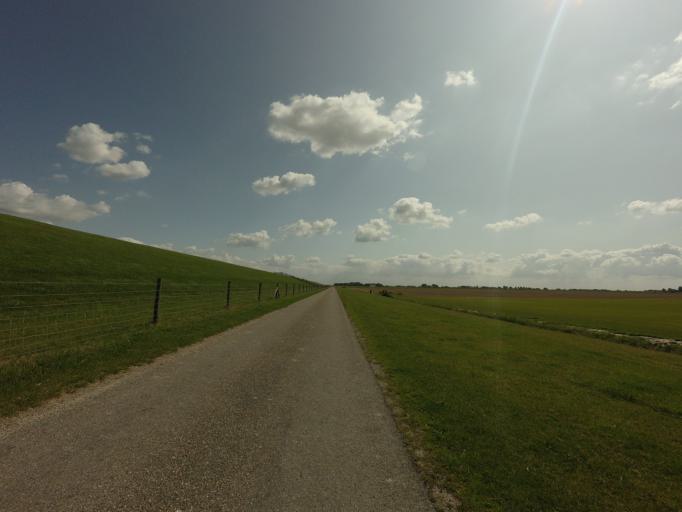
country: NL
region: Friesland
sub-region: Gemeente Ferwerderadiel
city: Hallum
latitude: 53.3214
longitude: 5.7460
